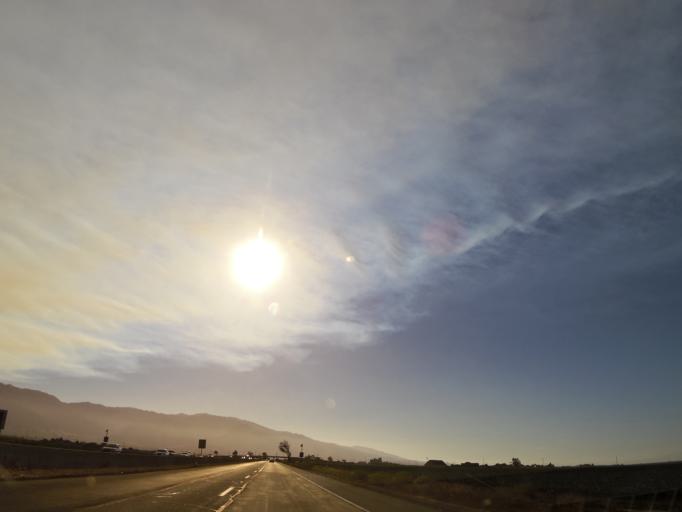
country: US
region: California
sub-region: Monterey County
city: Gonzales
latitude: 36.5221
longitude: -121.4520
